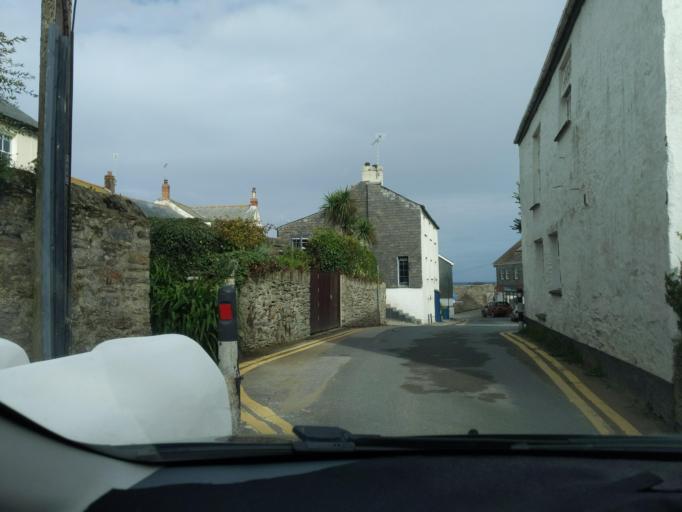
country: GB
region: England
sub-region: Cornwall
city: Mevagissey
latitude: 50.2403
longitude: -4.7892
